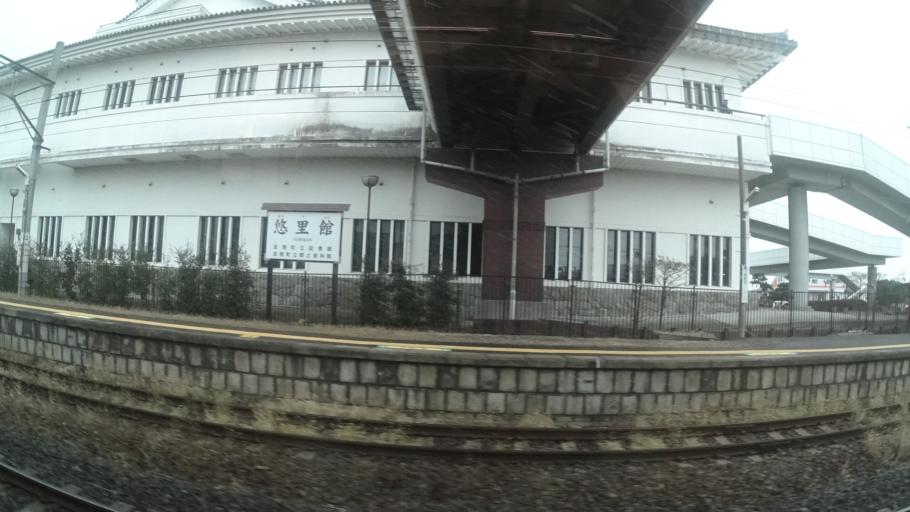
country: JP
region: Miyagi
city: Watari
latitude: 38.0399
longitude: 140.8613
